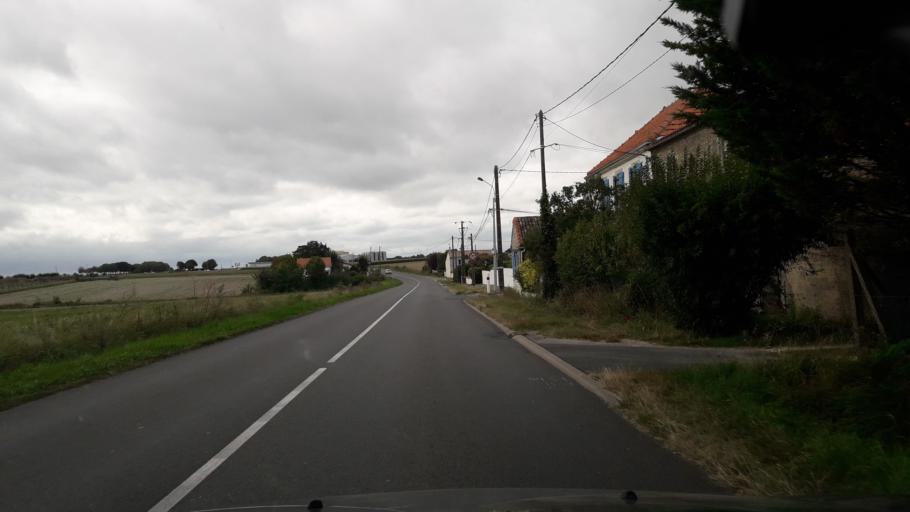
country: FR
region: Poitou-Charentes
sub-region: Departement de la Charente-Maritime
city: Saint-Sulpice-de-Royan
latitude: 45.6800
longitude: -0.9908
